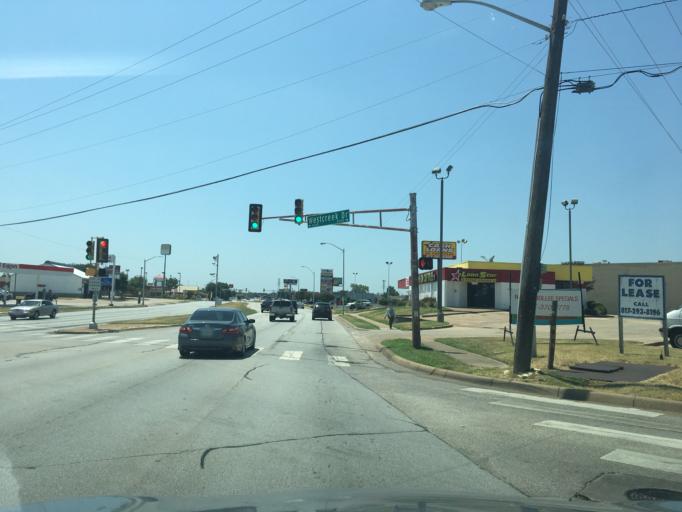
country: US
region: Texas
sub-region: Tarrant County
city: Edgecliff Village
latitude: 32.6555
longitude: -97.3618
